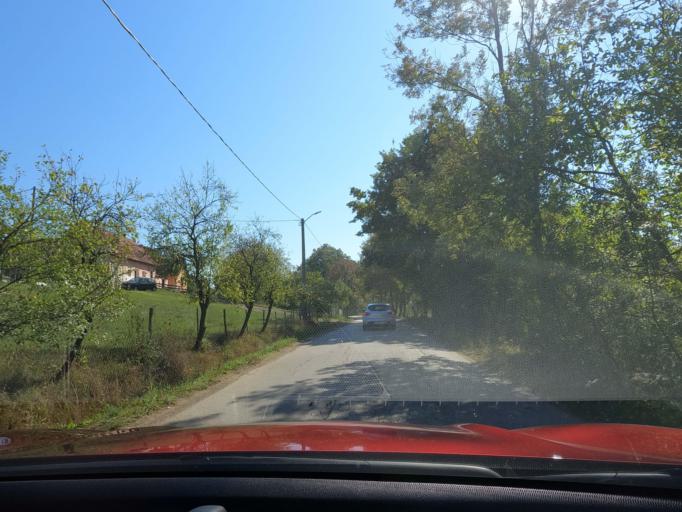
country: RS
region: Central Serbia
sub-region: Raski Okrug
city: Kraljevo
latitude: 43.7723
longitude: 20.6560
